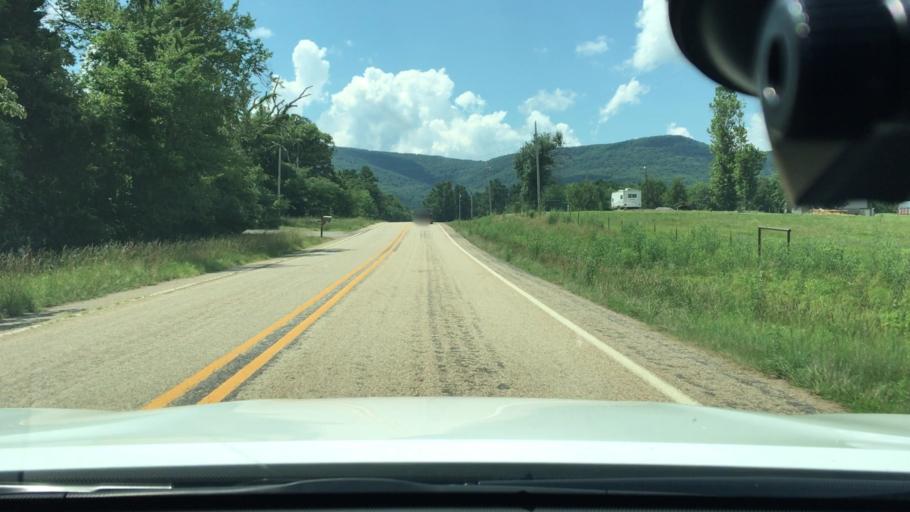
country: US
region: Arkansas
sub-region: Logan County
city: Paris
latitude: 35.2047
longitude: -93.6347
